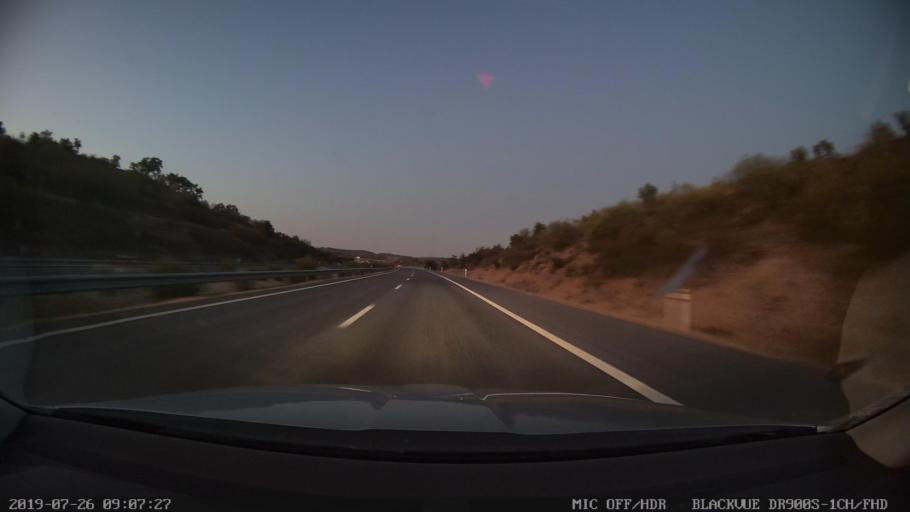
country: PT
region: Evora
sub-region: Estremoz
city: Estremoz
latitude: 38.7450
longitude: -7.7375
